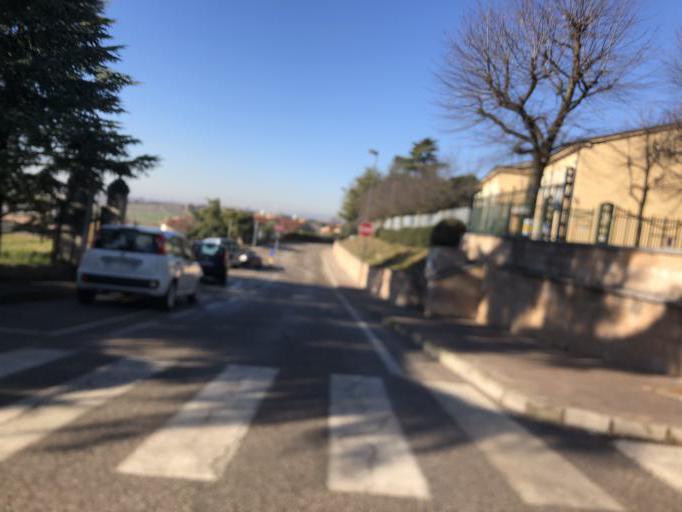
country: IT
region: Veneto
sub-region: Provincia di Verona
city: Sona
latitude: 45.4353
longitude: 10.8303
